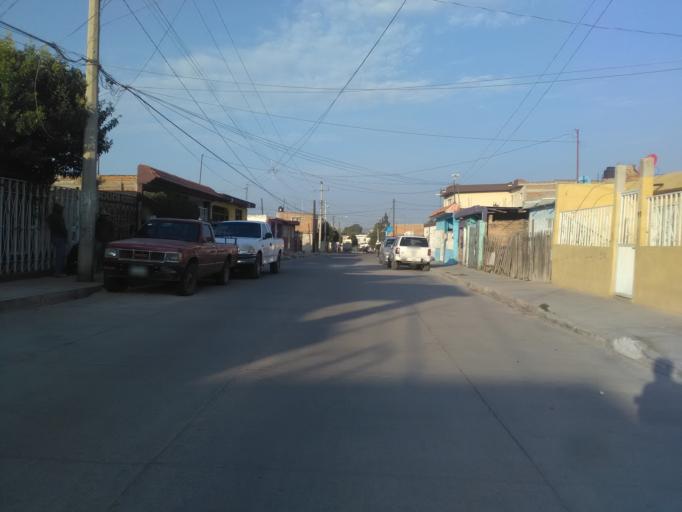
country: MX
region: Durango
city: Victoria de Durango
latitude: 24.0471
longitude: -104.6502
